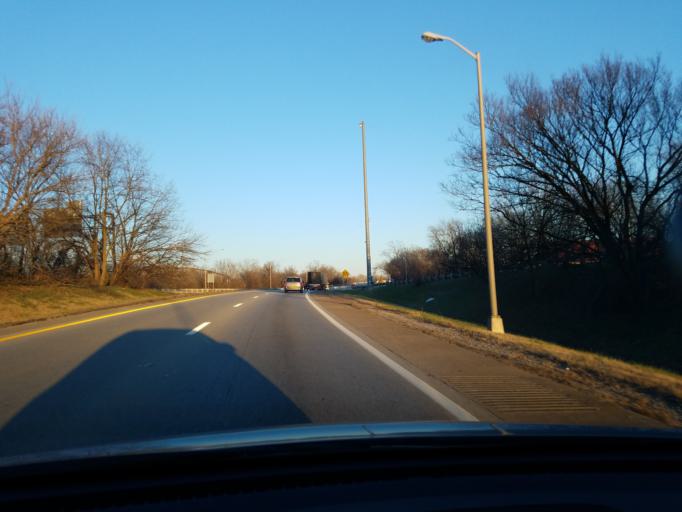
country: US
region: Indiana
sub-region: Floyd County
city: New Albany
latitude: 38.2768
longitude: -85.8075
